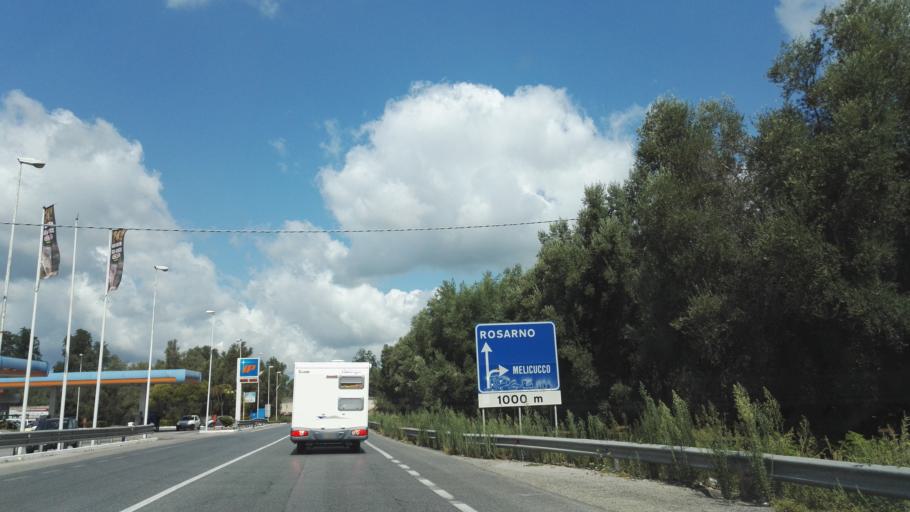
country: IT
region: Calabria
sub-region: Provincia di Reggio Calabria
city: Melicucco
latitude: 38.4224
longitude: 16.0631
